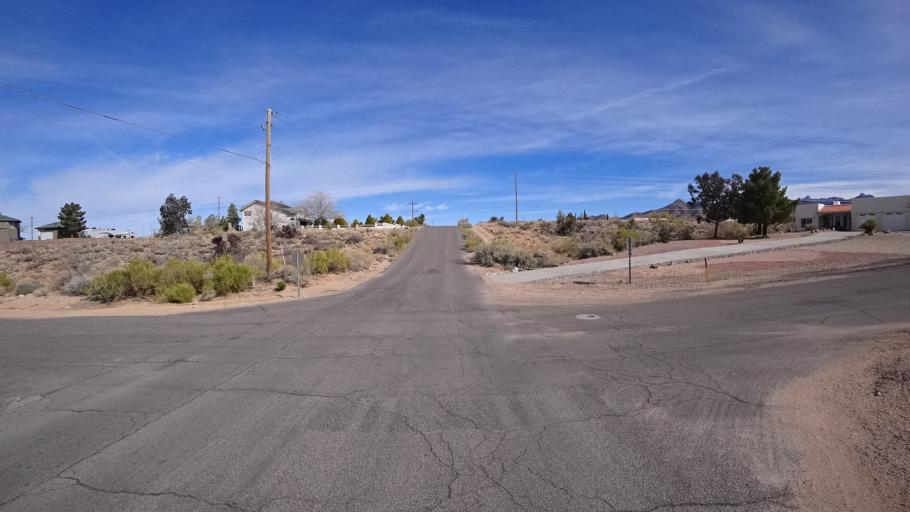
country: US
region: Arizona
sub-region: Mohave County
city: Kingman
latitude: 35.1877
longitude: -113.9860
